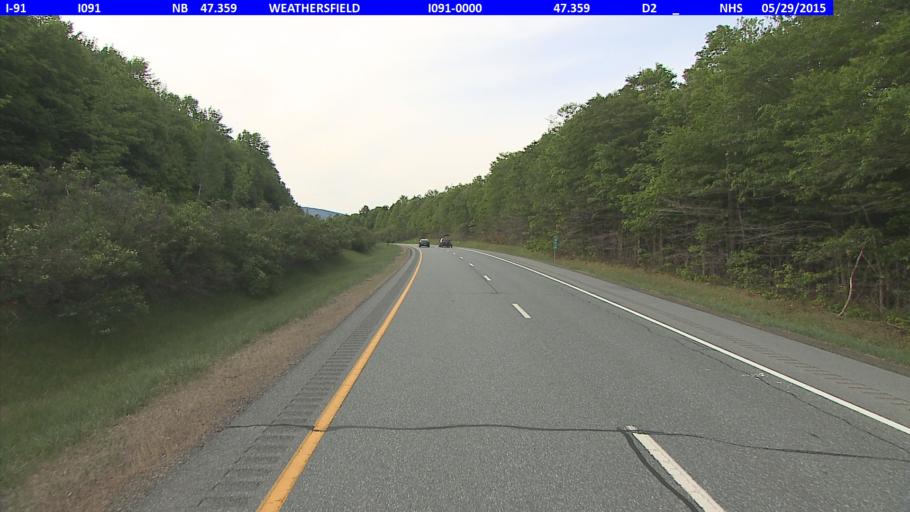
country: US
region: New Hampshire
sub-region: Sullivan County
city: Claremont
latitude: 43.3467
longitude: -72.4190
